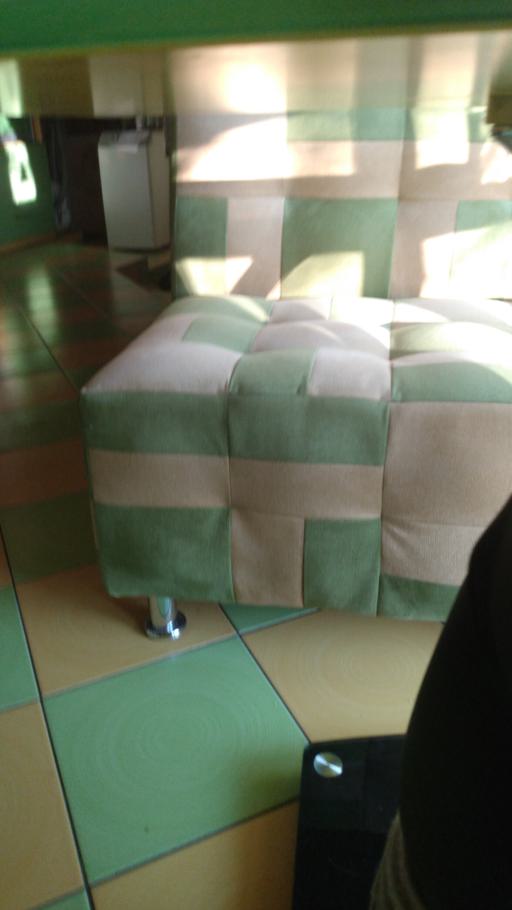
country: RU
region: Tverskaya
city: Vydropuzhsk
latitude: 57.4299
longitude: 34.7074
